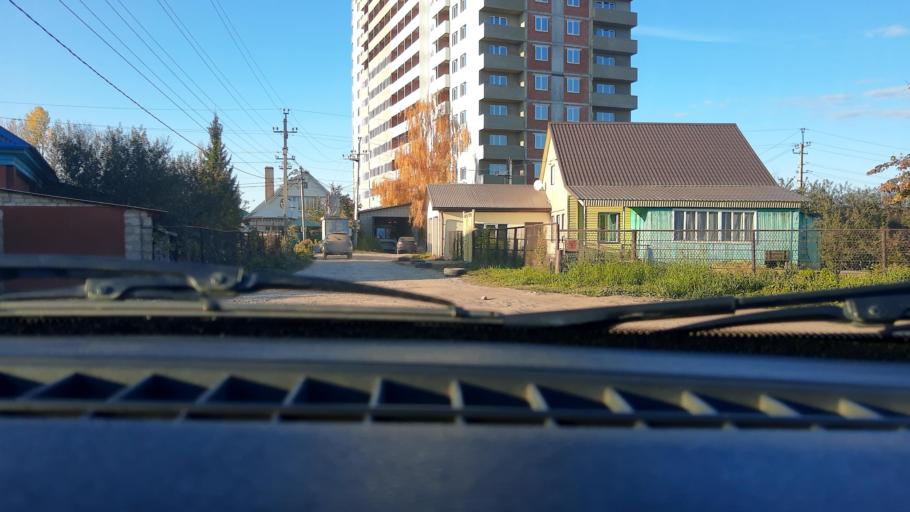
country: RU
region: Bashkortostan
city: Mikhaylovka
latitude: 54.7948
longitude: 55.8788
